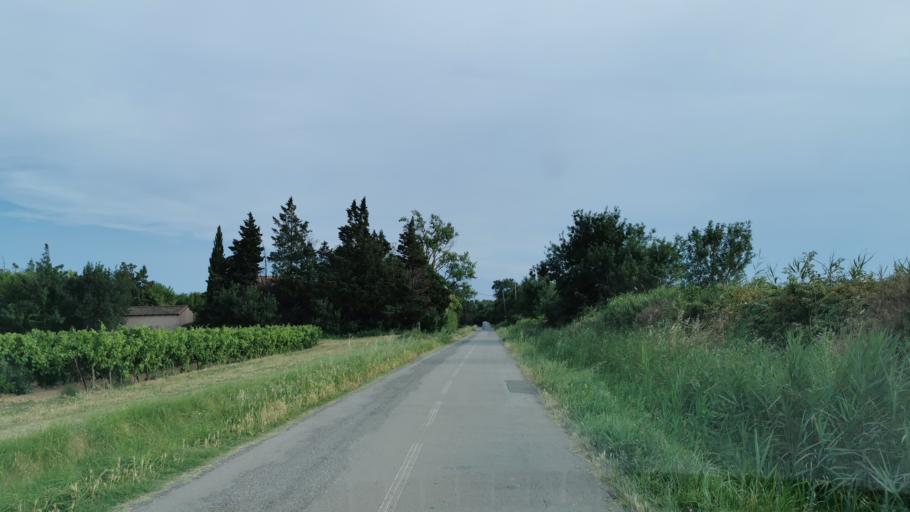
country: FR
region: Languedoc-Roussillon
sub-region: Departement de l'Aude
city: Narbonne
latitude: 43.2108
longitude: 2.9993
